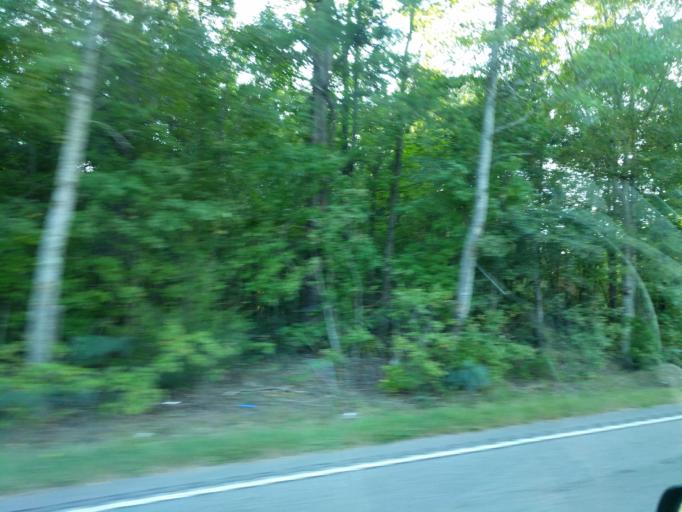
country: US
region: South Carolina
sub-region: Anderson County
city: Williamston
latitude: 34.6546
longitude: -82.4920
